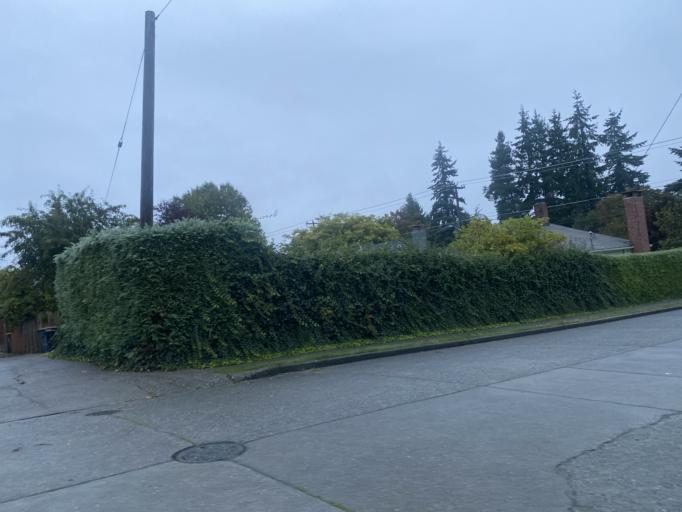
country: US
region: Washington
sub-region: King County
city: Seattle
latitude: 47.6431
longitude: -122.4030
